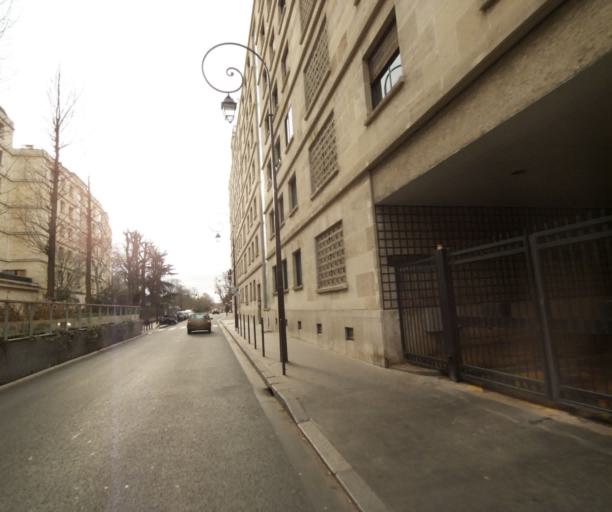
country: FR
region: Ile-de-France
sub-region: Departement des Hauts-de-Seine
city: Puteaux
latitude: 48.8765
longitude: 2.2505
